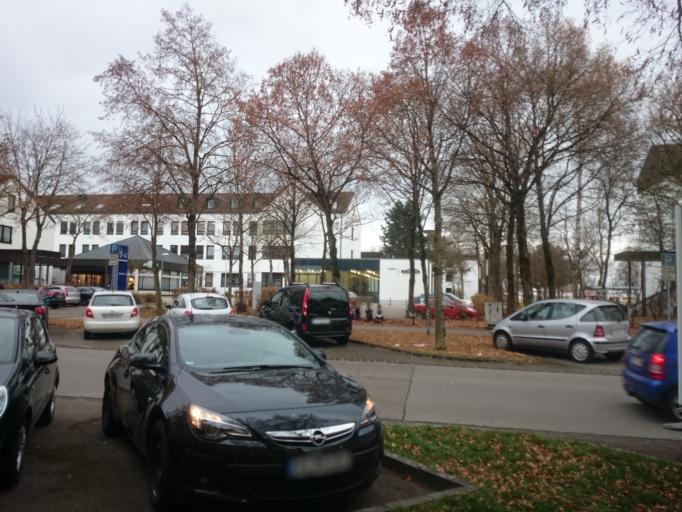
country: DE
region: Bavaria
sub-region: Swabia
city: Augsburg
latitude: 48.3307
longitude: 10.9009
